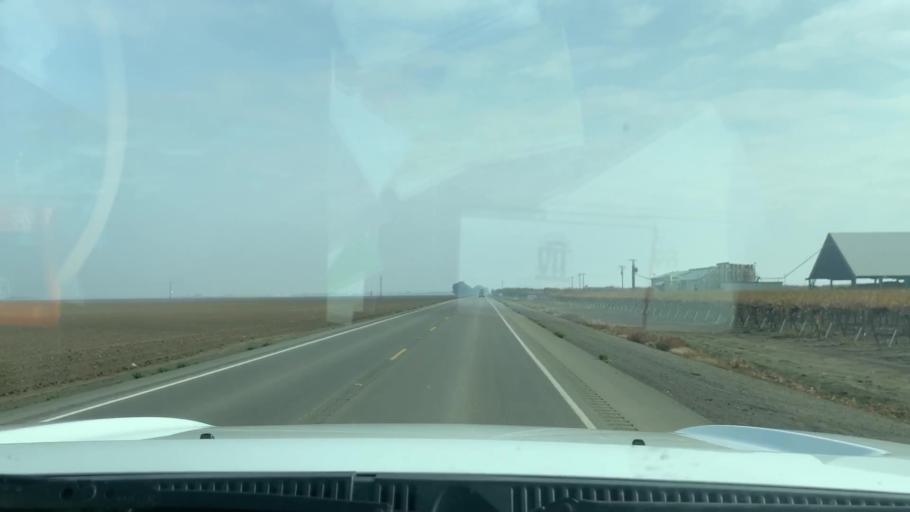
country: US
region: California
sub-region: Kings County
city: Lemoore Station
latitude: 36.2555
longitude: -119.9546
